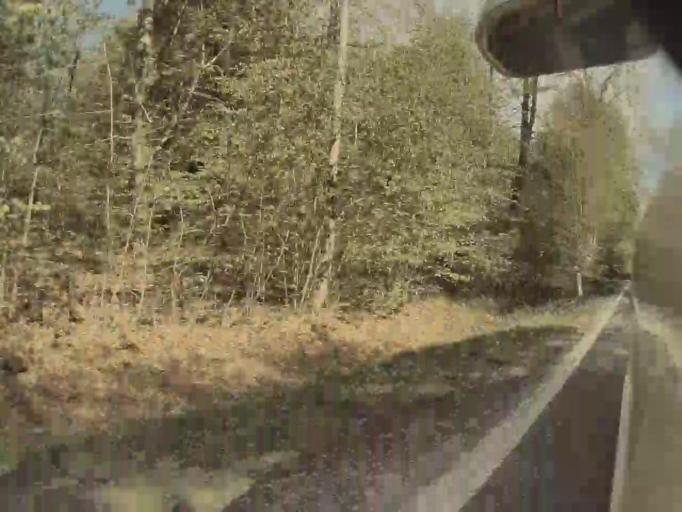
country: BE
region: Wallonia
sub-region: Province du Luxembourg
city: Tellin
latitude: 50.0376
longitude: 5.2079
